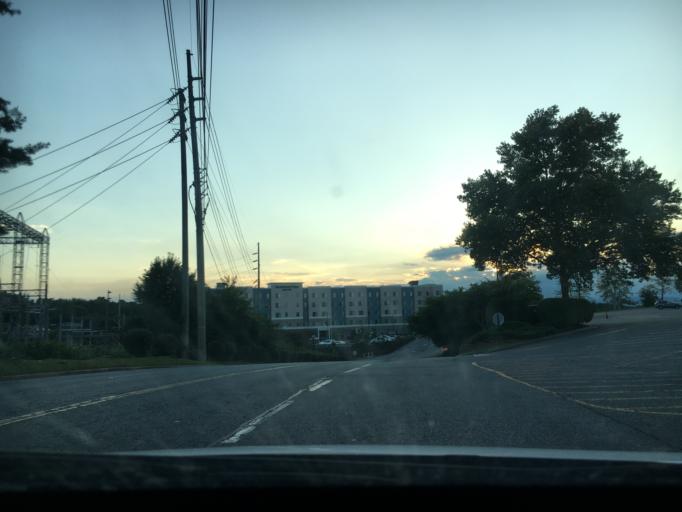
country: US
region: Virginia
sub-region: City of Lynchburg
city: West Lynchburg
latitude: 37.3624
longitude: -79.1787
